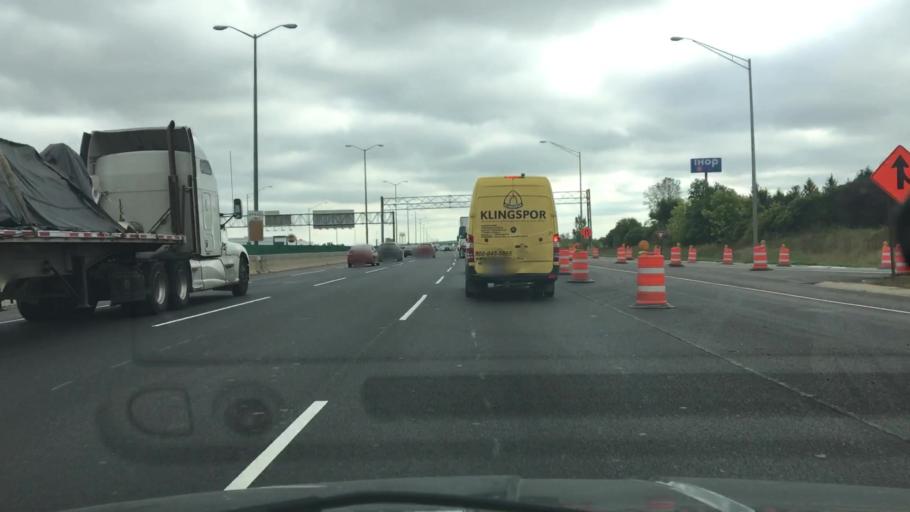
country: US
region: Illinois
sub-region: DuPage County
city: Woodridge
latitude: 41.7223
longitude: -88.0344
